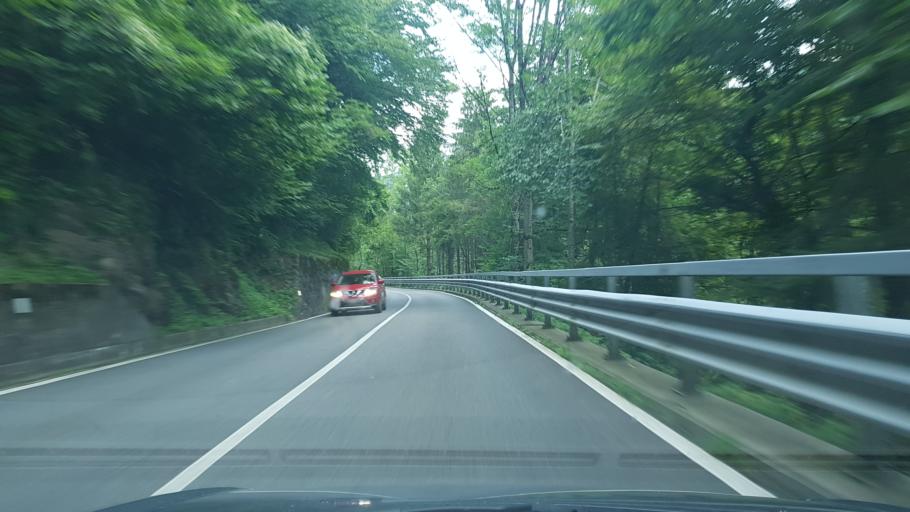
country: IT
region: Friuli Venezia Giulia
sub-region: Provincia di Udine
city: Rigolato
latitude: 46.5448
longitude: 12.8606
